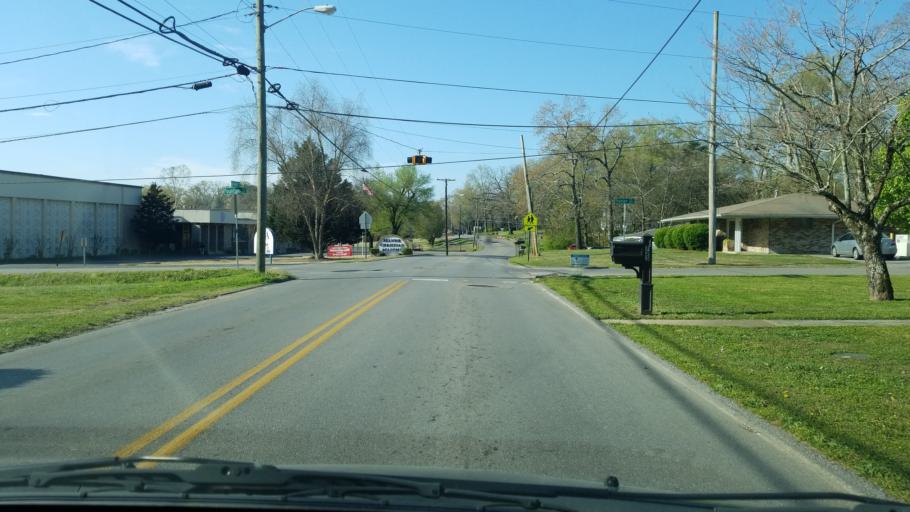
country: US
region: Tennessee
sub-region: Hamilton County
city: East Ridge
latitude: 35.0048
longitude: -85.2445
